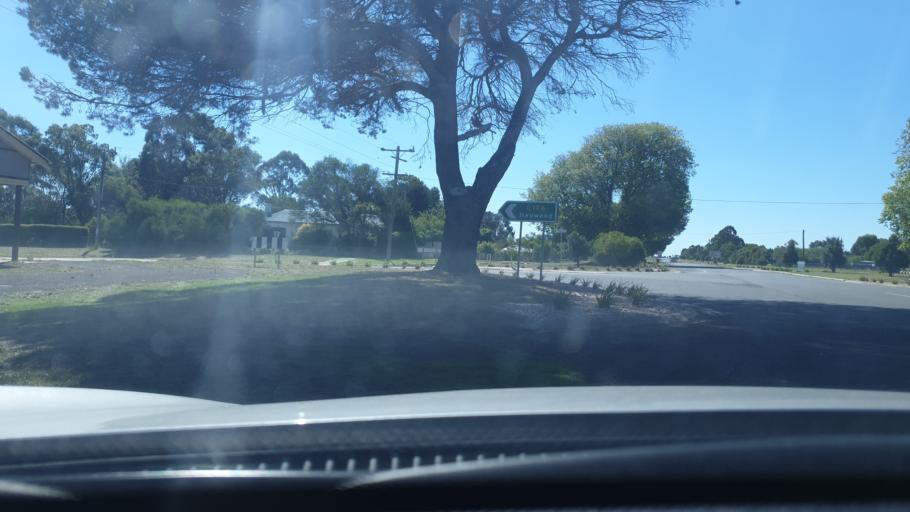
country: AU
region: Victoria
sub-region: Warrnambool
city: Warrnambool
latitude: -38.1850
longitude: 142.4315
